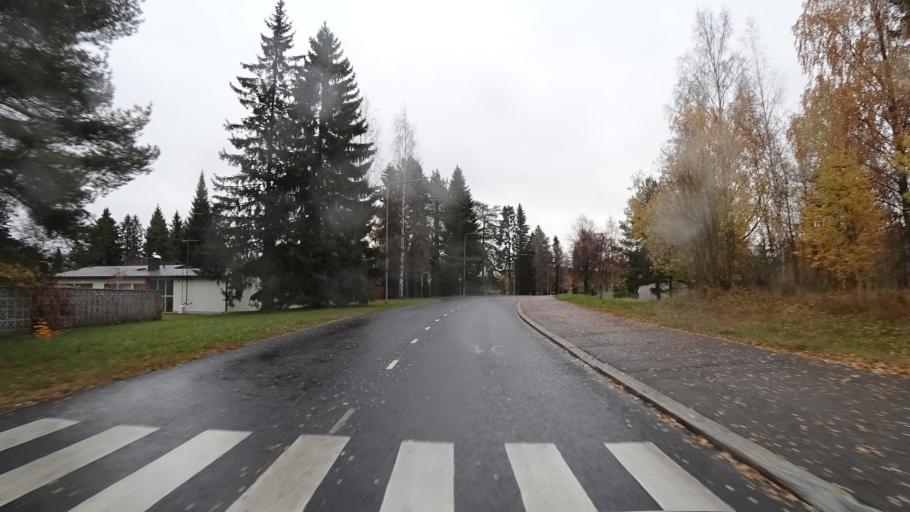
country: FI
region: Northern Savo
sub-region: Kuopio
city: Kuopio
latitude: 62.9295
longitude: 27.6872
